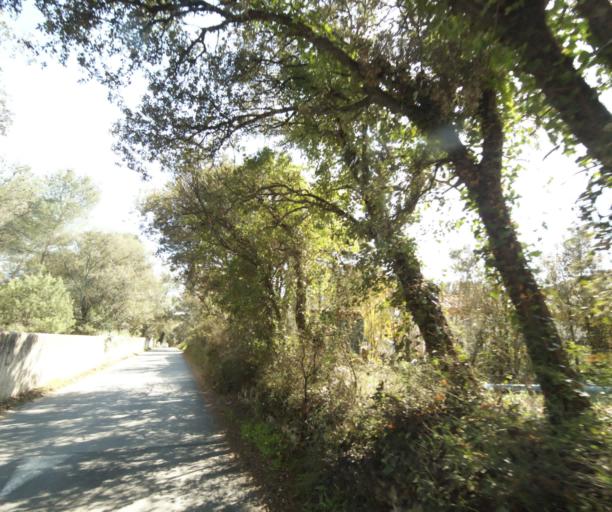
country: FR
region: Languedoc-Roussillon
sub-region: Departement de l'Herault
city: Castries
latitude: 43.6914
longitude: 3.9991
